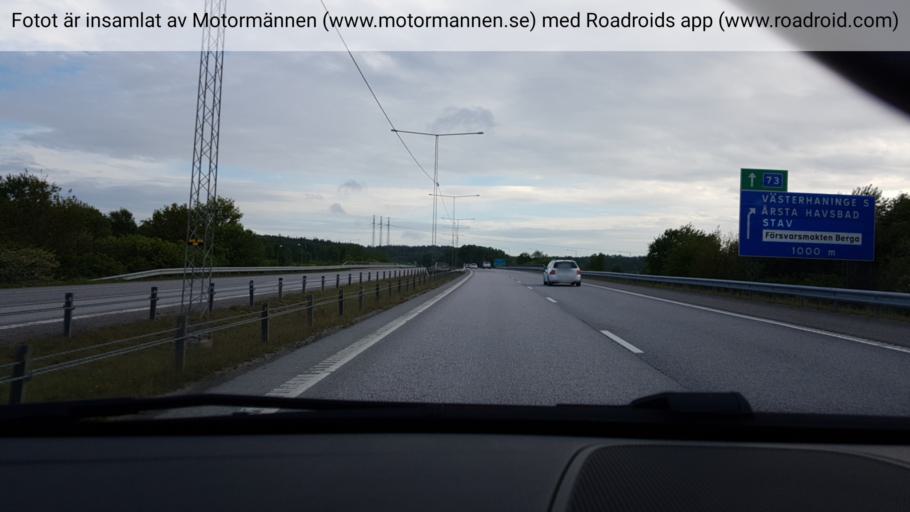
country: SE
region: Stockholm
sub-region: Haninge Kommun
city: Jordbro
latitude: 59.1234
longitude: 18.1346
